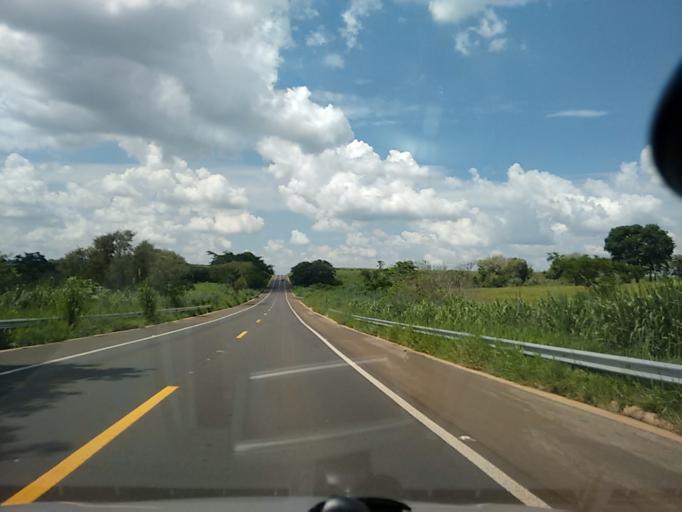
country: BR
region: Sao Paulo
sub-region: Osvaldo Cruz
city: Osvaldo Cruz
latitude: -21.8909
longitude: -50.8733
